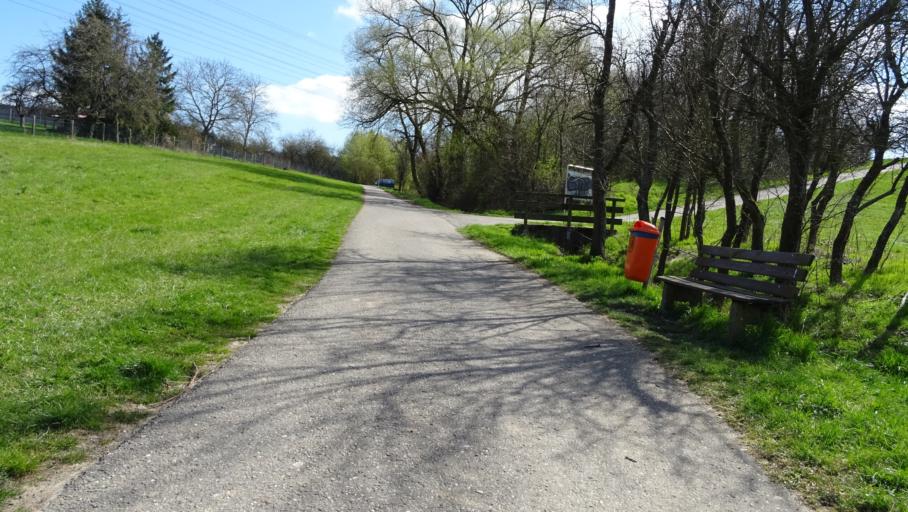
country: DE
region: Baden-Wuerttemberg
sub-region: Karlsruhe Region
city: Neckarzimmern
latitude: 49.3331
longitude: 9.1142
